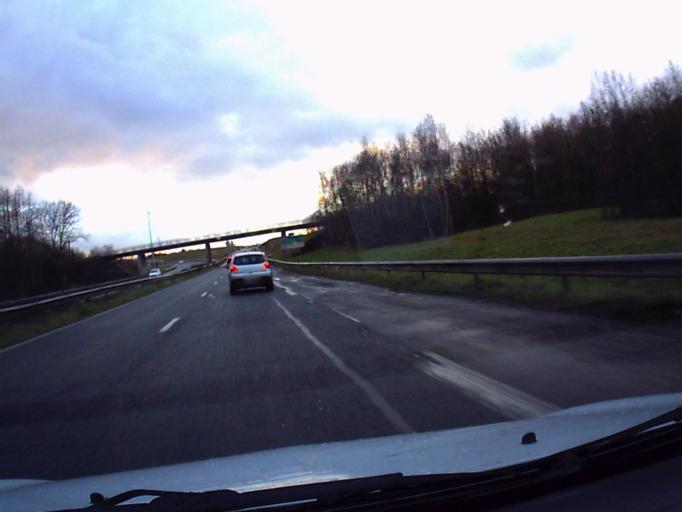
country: FR
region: Brittany
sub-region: Departement d'Ille-et-Vilaine
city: Vezin-le-Coquet
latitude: 48.1229
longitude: -1.7314
